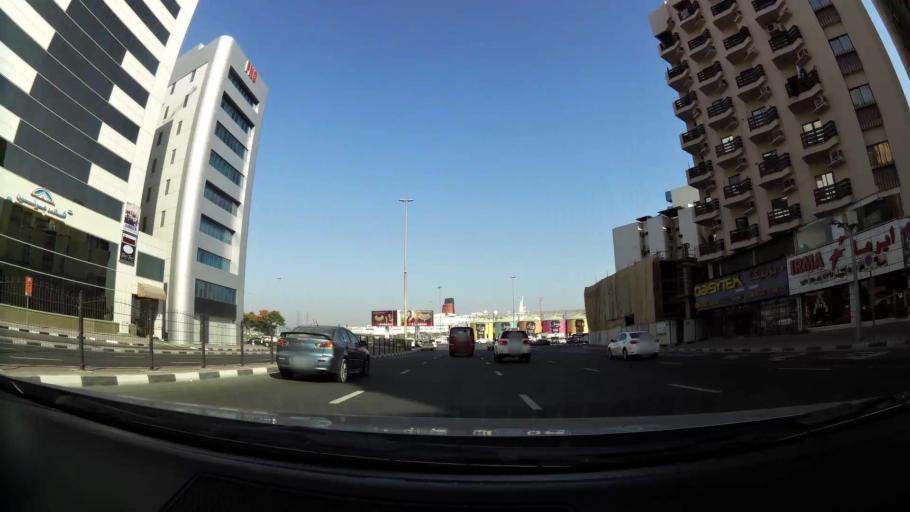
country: AE
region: Ash Shariqah
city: Sharjah
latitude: 25.2604
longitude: 55.2857
